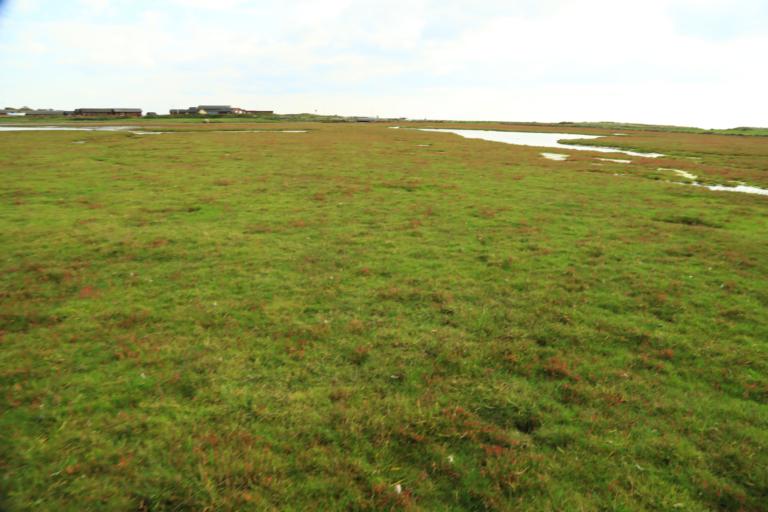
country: SE
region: Halland
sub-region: Varbergs Kommun
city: Traslovslage
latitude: 57.0302
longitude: 12.3078
